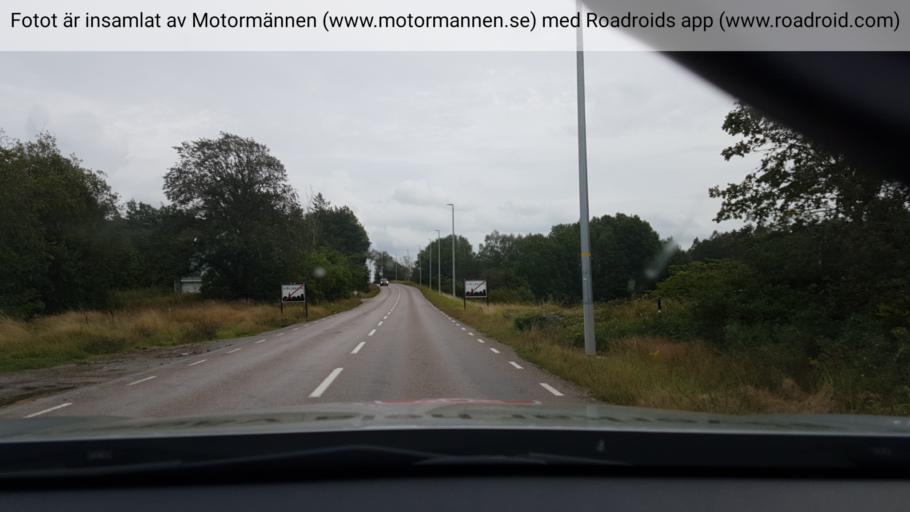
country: SE
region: Vaestra Goetaland
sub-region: Tanums Kommun
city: Grebbestad
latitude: 58.5980
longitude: 11.2959
